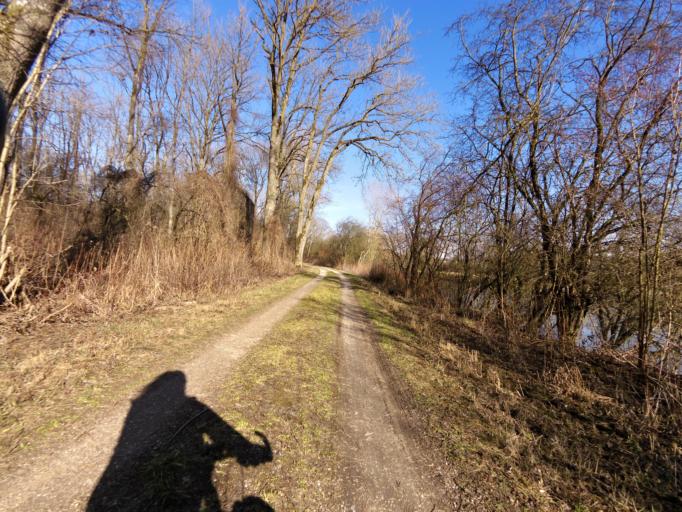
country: DE
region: Bavaria
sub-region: Lower Bavaria
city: Eching
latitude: 48.5075
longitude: 12.0695
